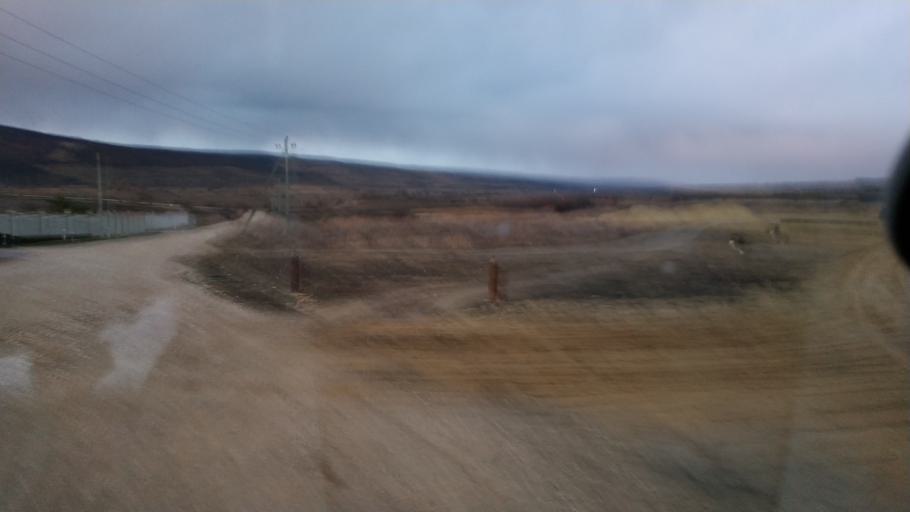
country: MD
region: Taraclia
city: Telenesti
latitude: 47.3867
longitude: 28.3269
